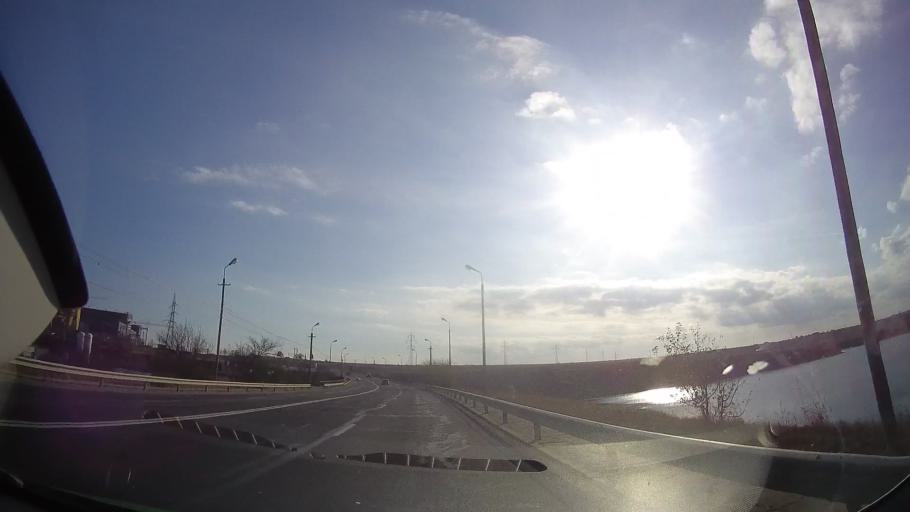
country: RO
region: Constanta
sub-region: Municipiul Mangalia
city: Mangalia
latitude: 43.8015
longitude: 28.5595
